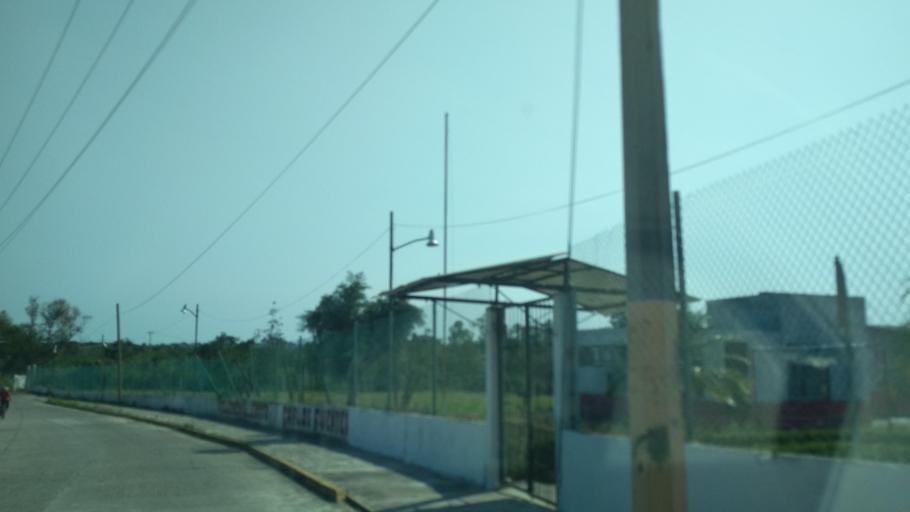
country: MX
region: Veracruz
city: Gutierrez Zamora
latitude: 20.4131
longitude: -97.1871
